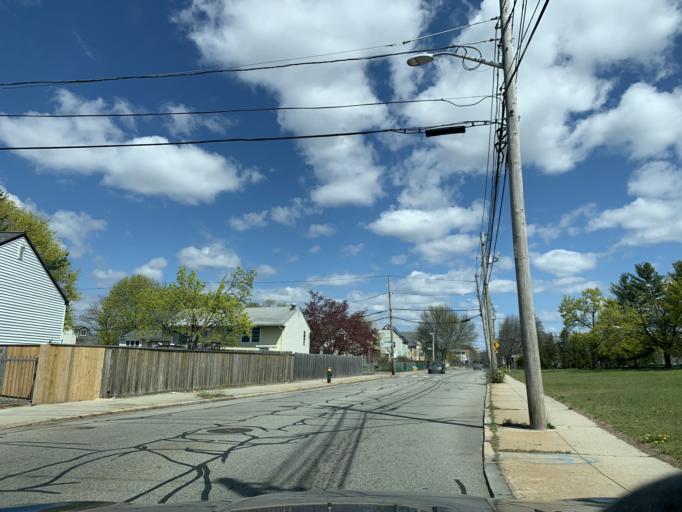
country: US
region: Rhode Island
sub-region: Providence County
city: Providence
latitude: 41.8083
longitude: -71.4159
